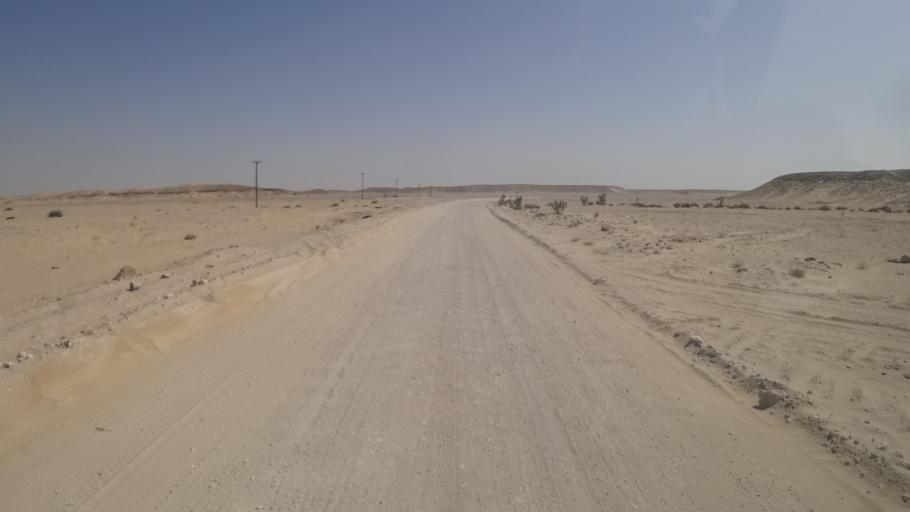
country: YE
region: Al Mahrah
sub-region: Shahan
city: Shihan as Sufla
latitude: 17.8719
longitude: 52.6093
